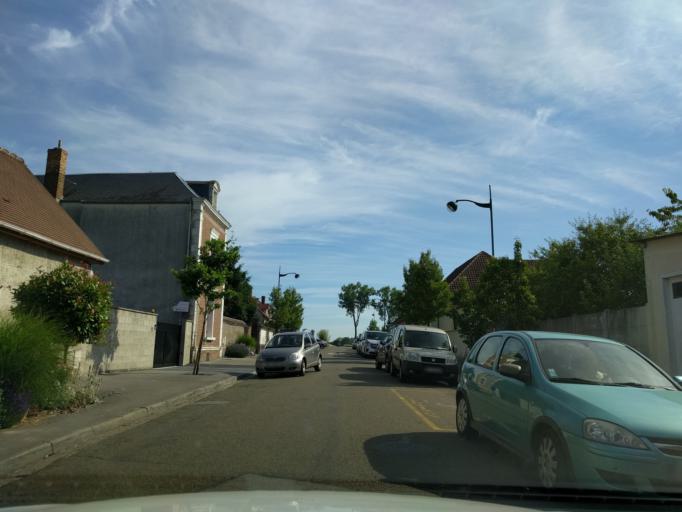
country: FR
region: Picardie
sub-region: Departement de l'Oise
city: Tille
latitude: 49.4661
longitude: 2.1100
